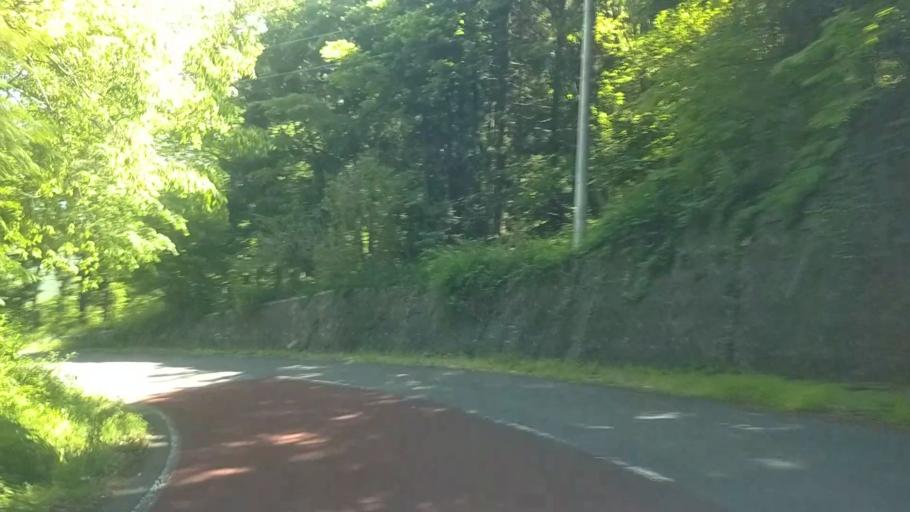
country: JP
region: Yamanashi
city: Nirasaki
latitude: 35.8552
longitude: 138.4326
